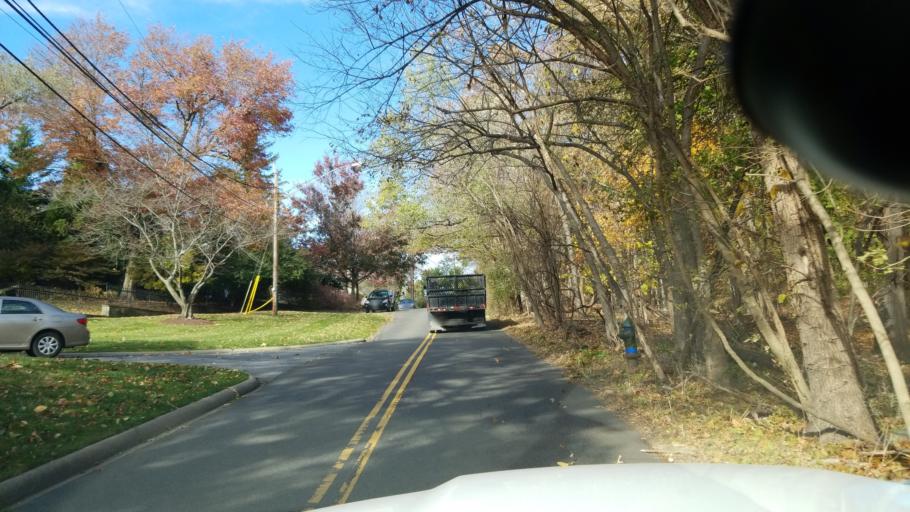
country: US
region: Maryland
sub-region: Montgomery County
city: Chevy Chase
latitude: 38.9593
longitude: -77.0561
